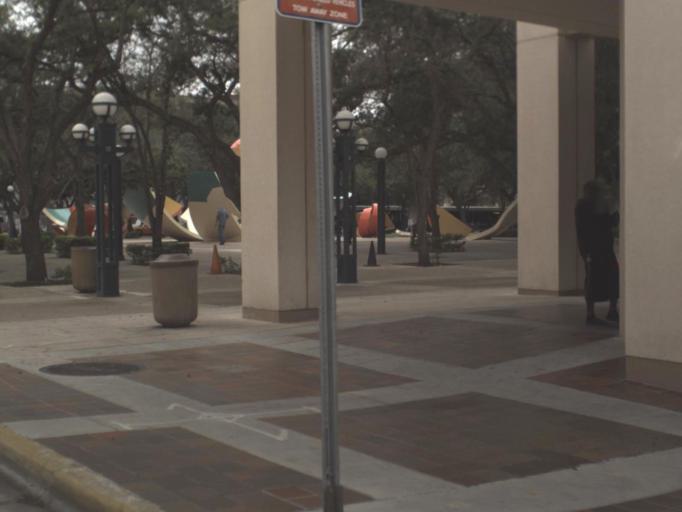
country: US
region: Florida
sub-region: Miami-Dade County
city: Miami
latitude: 25.7751
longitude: -80.1969
